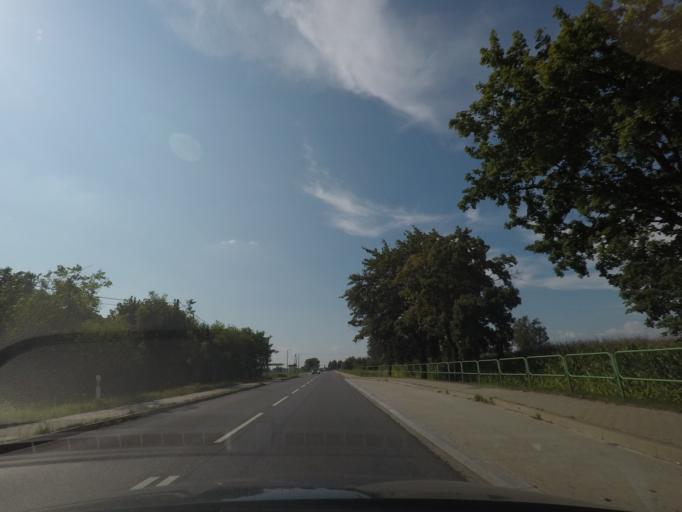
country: PL
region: Silesian Voivodeship
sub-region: Powiat pszczynski
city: Radostowice
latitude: 50.0060
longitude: 18.8707
